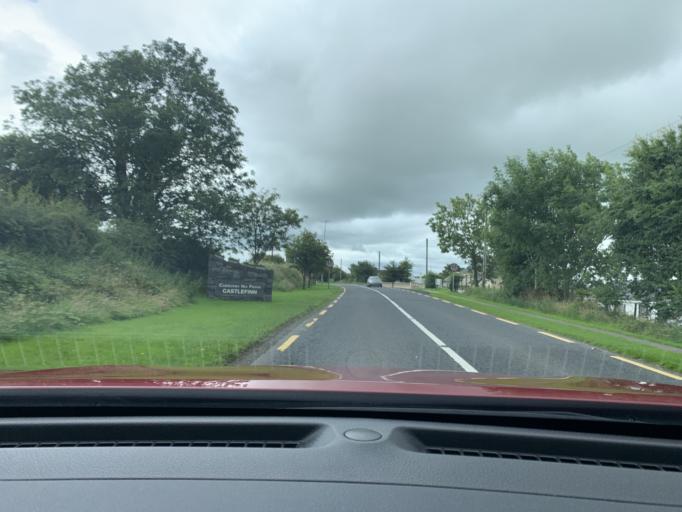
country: IE
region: Ulster
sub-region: County Donegal
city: Raphoe
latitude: 54.8027
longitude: -7.6012
